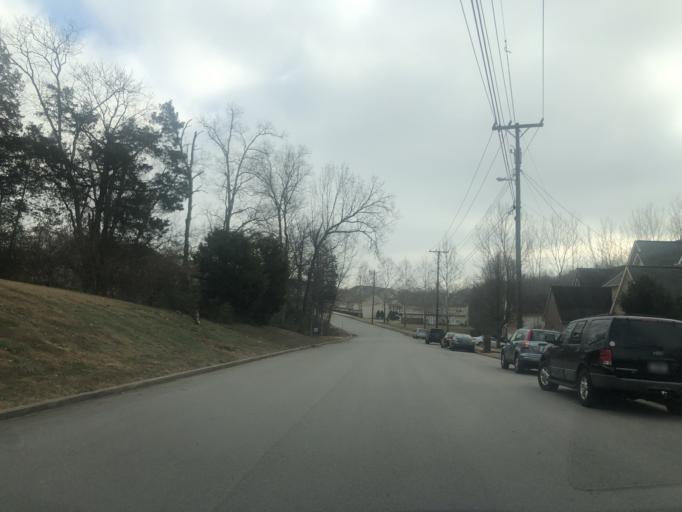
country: US
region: Tennessee
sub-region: Rutherford County
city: La Vergne
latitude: 36.0661
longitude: -86.6497
